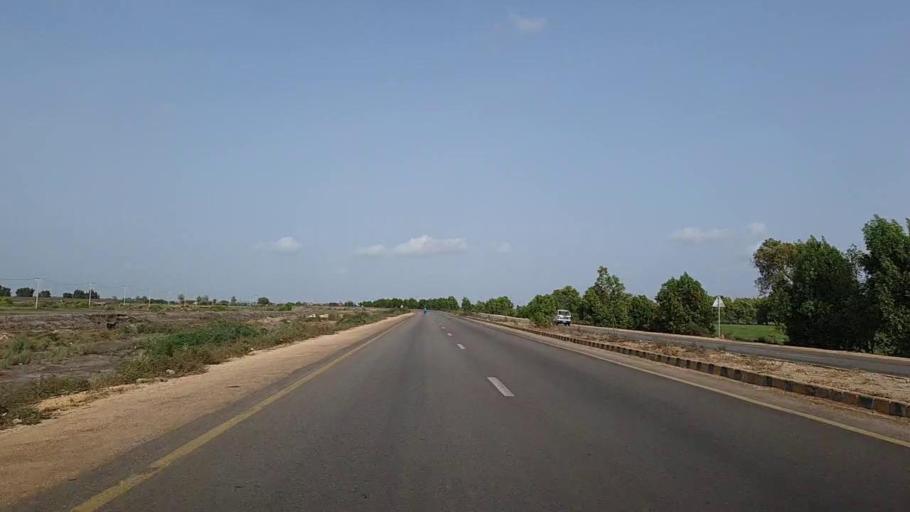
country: PK
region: Sindh
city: Thatta
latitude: 24.7429
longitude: 67.7967
